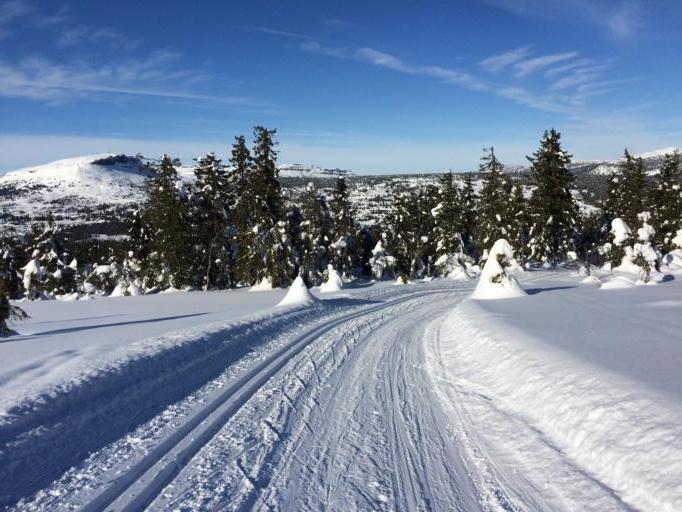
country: NO
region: Oppland
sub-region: Gausdal
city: Segalstad bru
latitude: 61.3122
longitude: 10.1042
